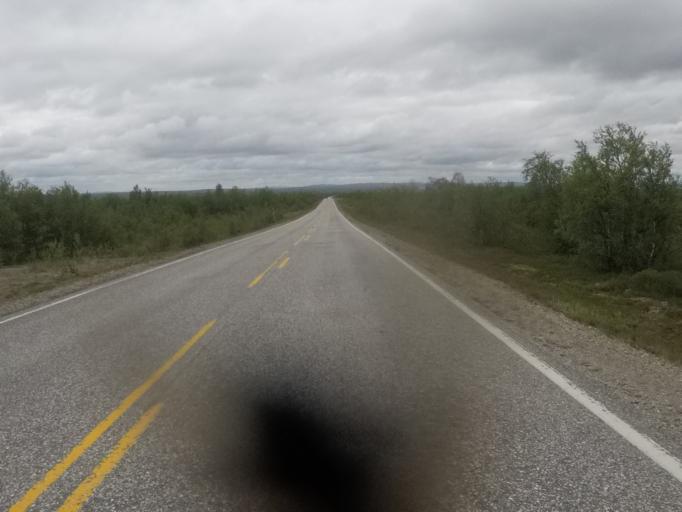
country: NO
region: Finnmark Fylke
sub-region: Kautokeino
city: Kautokeino
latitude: 68.7283
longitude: 23.3081
